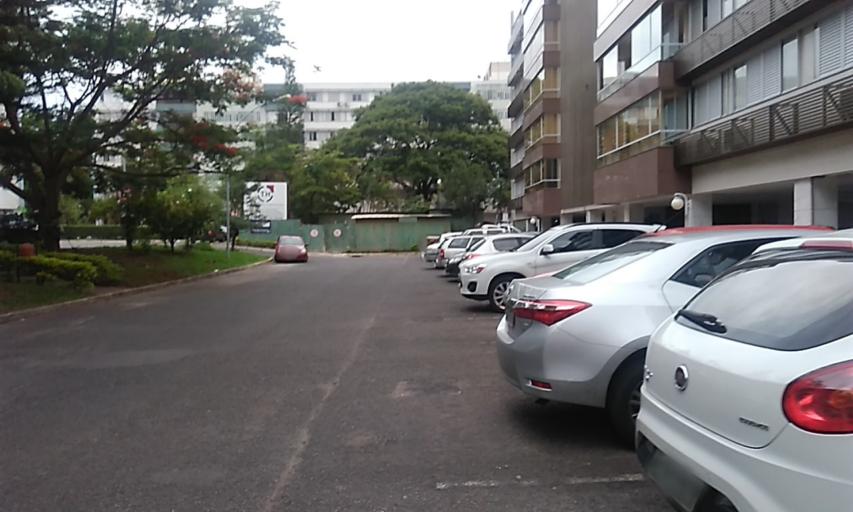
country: BR
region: Federal District
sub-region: Brasilia
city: Brasilia
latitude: -15.7761
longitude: -47.8867
